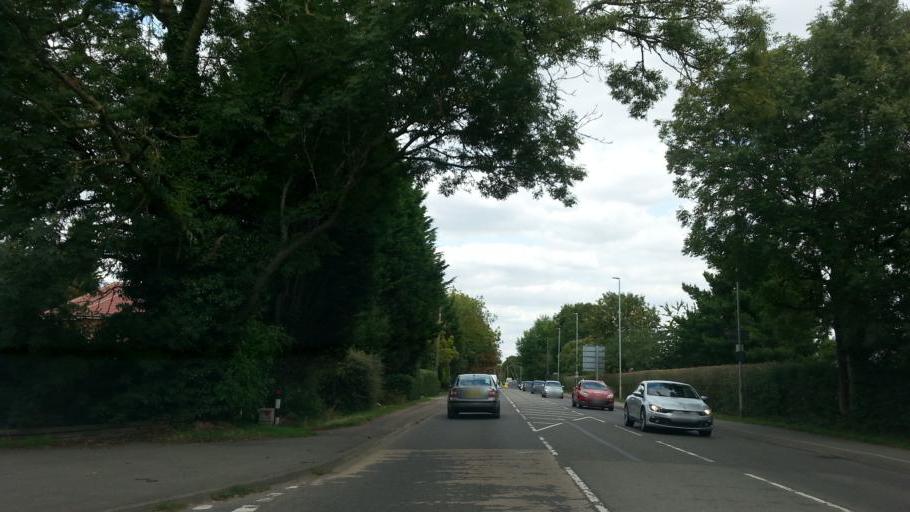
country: GB
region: England
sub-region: Leicestershire
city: Kirby Muxloe
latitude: 52.6202
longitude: -1.2293
